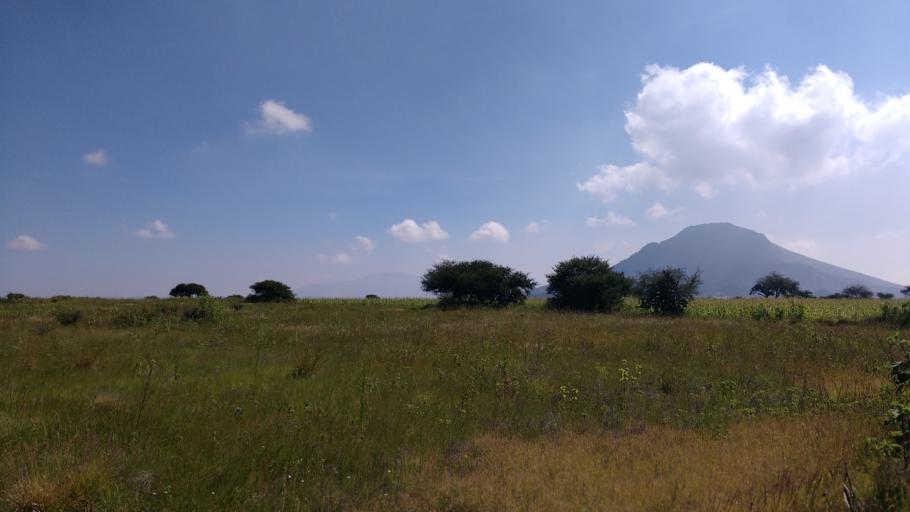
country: MX
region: Hidalgo
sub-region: Tezontepec de Aldama
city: Tenango
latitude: 20.2434
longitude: -99.2676
